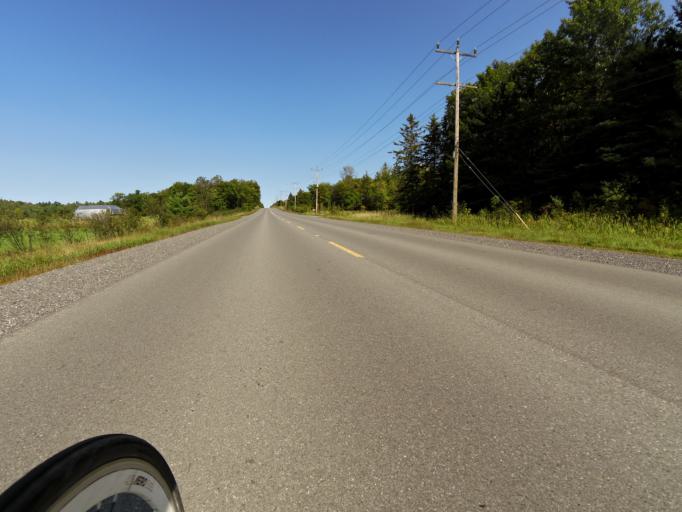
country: CA
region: Ontario
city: Arnprior
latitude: 45.4185
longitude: -76.1455
